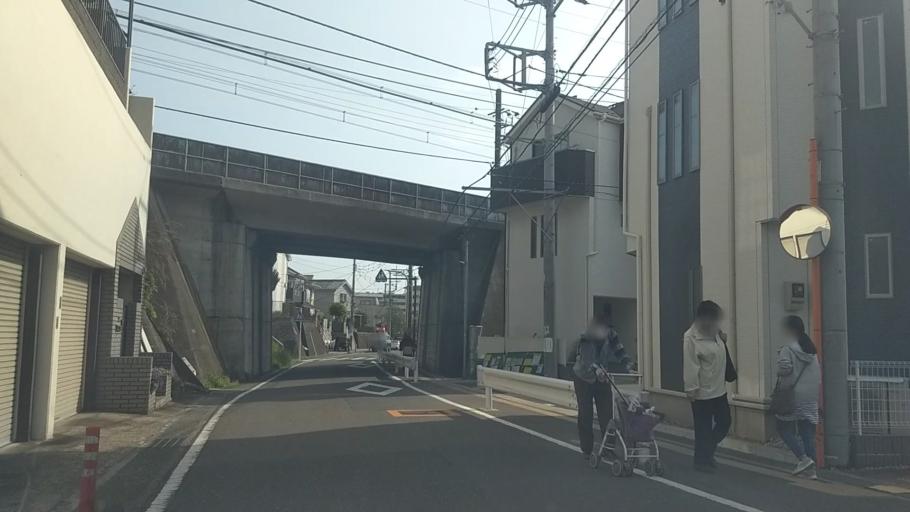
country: JP
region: Kanagawa
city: Kamakura
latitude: 35.3694
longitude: 139.5546
